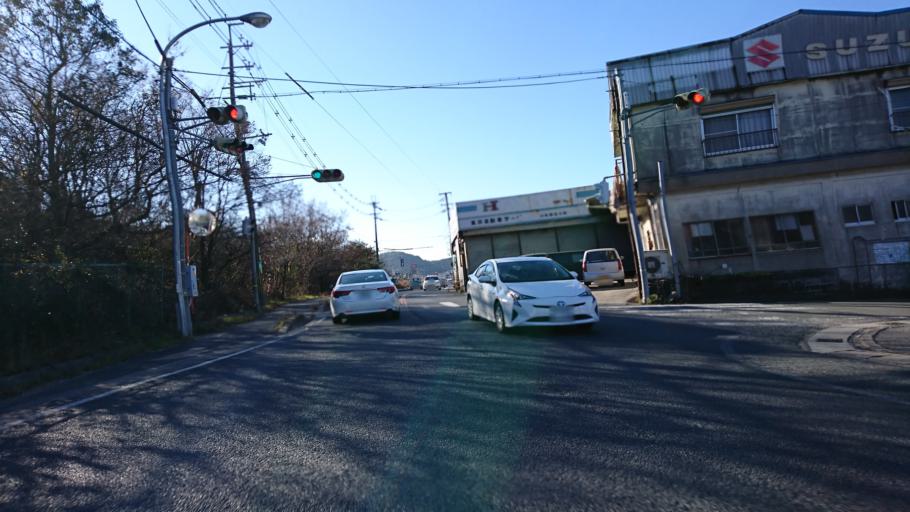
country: JP
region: Hyogo
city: Kakogawacho-honmachi
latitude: 34.8118
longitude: 134.8364
